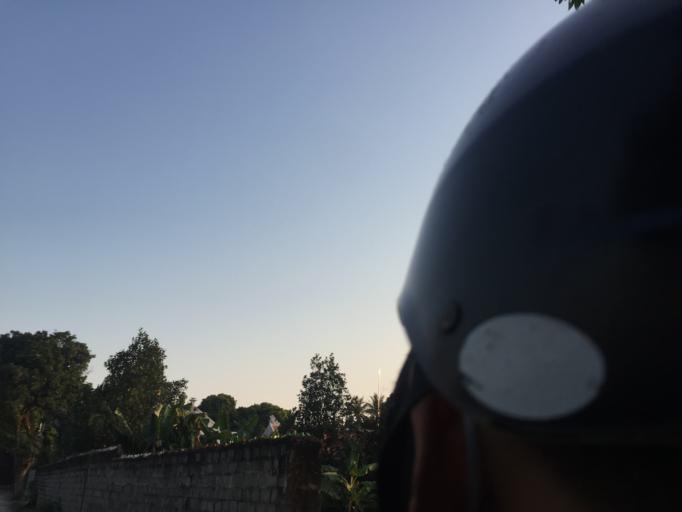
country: VN
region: Ha Noi
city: Chuc Son
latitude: 20.9070
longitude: 105.7239
